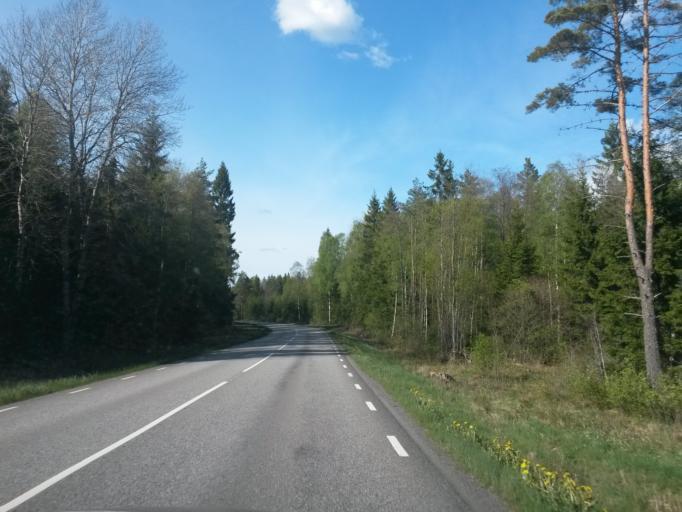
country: SE
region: Vaestra Goetaland
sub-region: Herrljunga Kommun
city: Herrljunga
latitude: 58.0266
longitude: 13.0482
